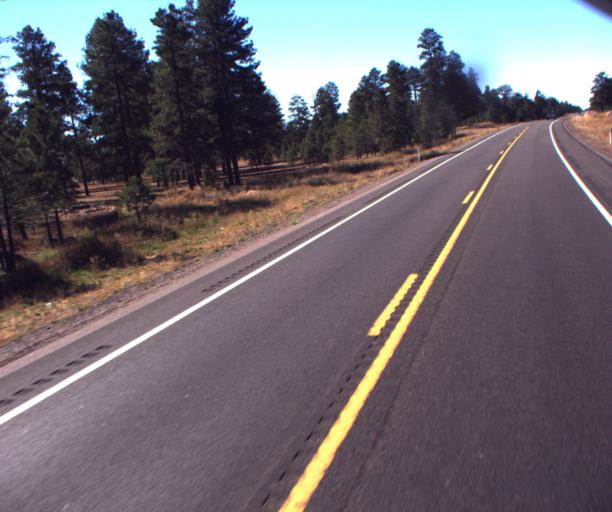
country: US
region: Arizona
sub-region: Apache County
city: Saint Michaels
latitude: 35.6859
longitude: -109.2398
